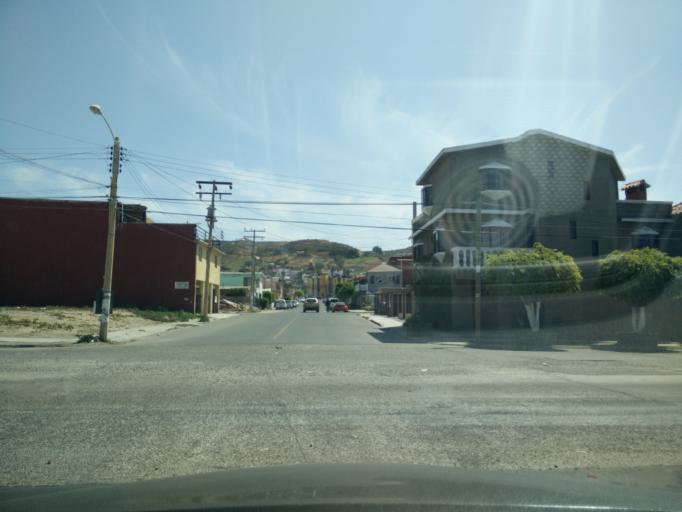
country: MX
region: Baja California
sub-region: Tijuana
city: La Esperanza [Granjas Familiares]
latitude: 32.5078
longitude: -117.1211
